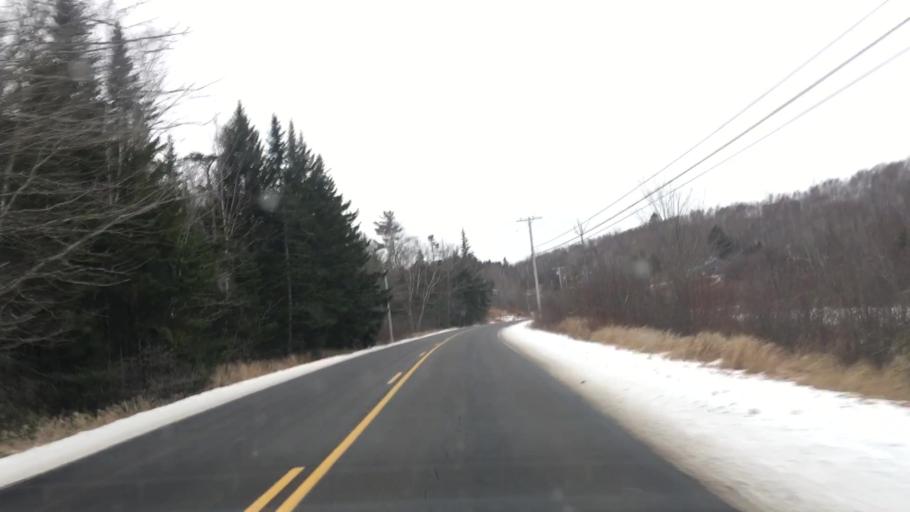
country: US
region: Maine
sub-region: Washington County
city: Machiasport
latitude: 44.7114
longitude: -67.3721
